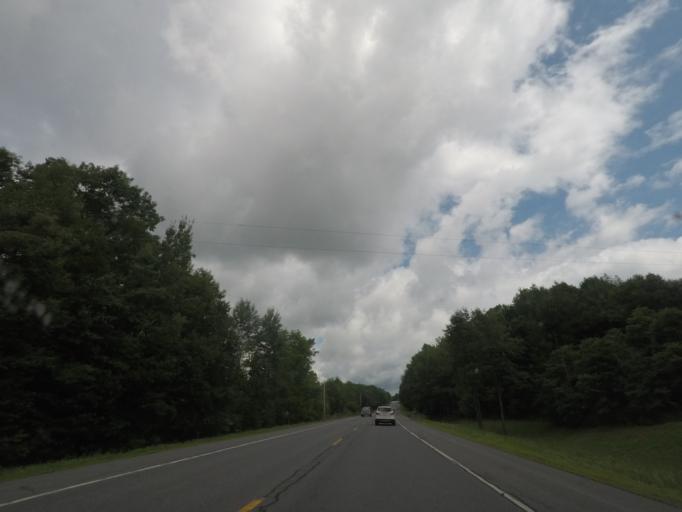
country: US
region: Massachusetts
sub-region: Berkshire County
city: Lanesborough
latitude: 42.5708
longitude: -73.3684
